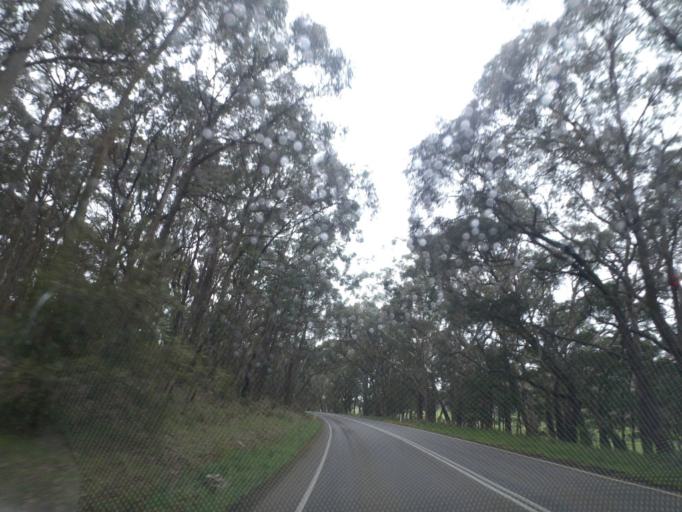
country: AU
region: Victoria
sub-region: Hume
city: Sunbury
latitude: -37.3494
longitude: 144.6575
